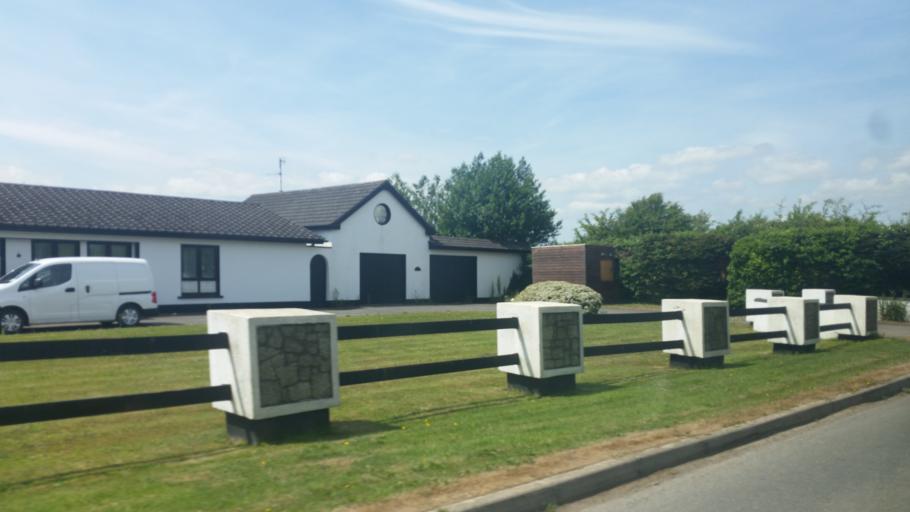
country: IE
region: Leinster
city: Lusk
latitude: 53.5335
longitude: -6.1776
